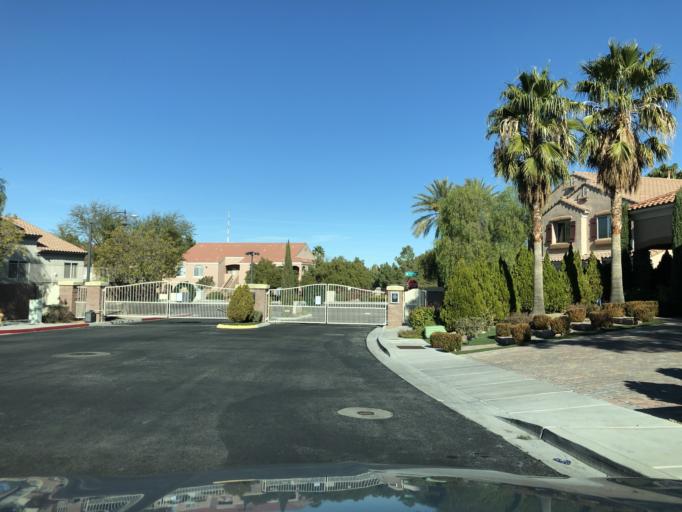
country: US
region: Nevada
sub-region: Clark County
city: Whitney
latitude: 35.9999
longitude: -115.0927
